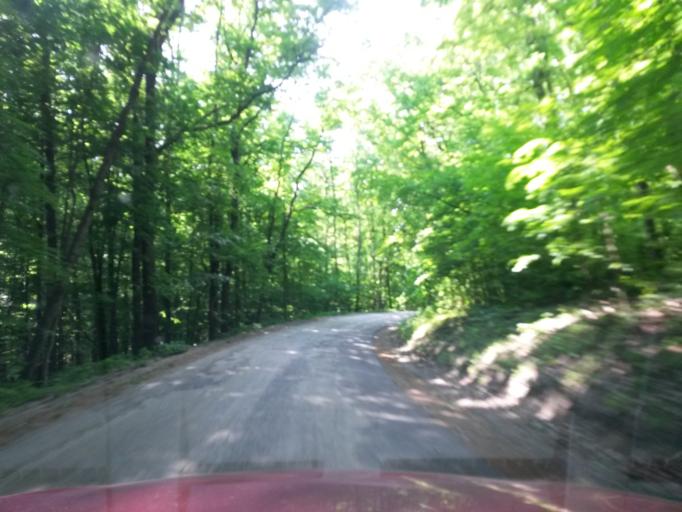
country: SK
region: Kosicky
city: Moldava nad Bodvou
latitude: 48.7191
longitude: 21.0318
